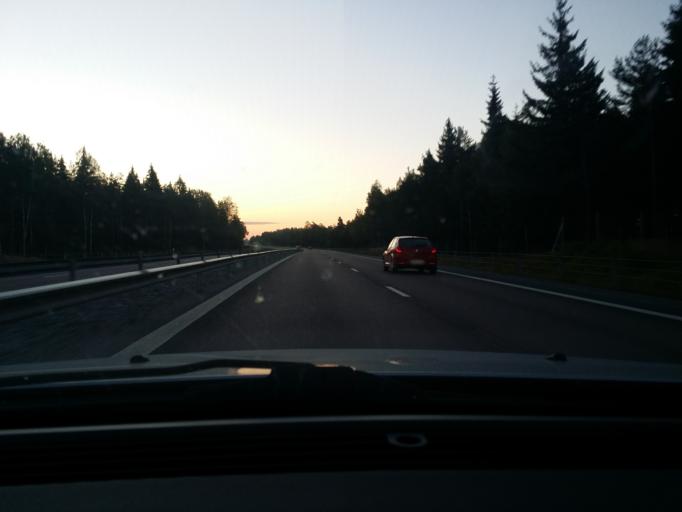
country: SE
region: Vaestmanland
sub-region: Vasteras
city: Tillberga
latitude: 59.6241
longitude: 16.6953
